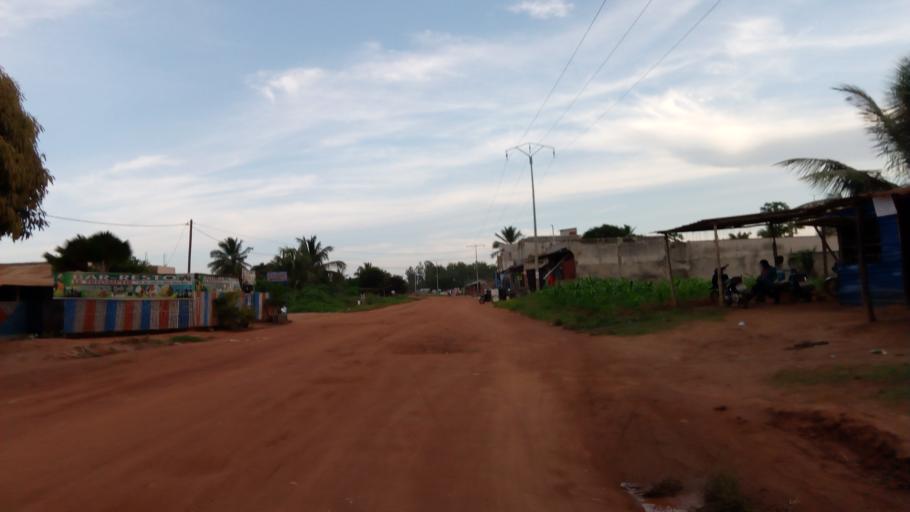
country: TG
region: Maritime
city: Lome
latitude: 6.2578
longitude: 1.1389
